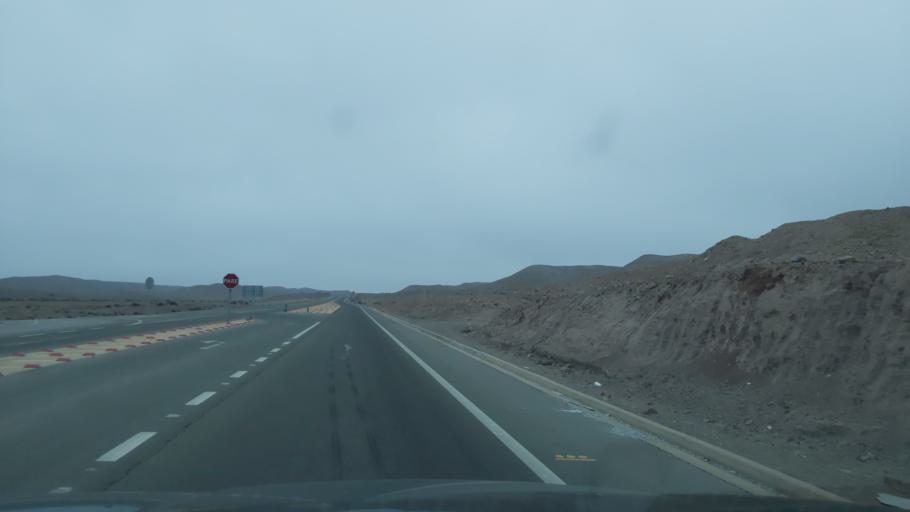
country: CL
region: Atacama
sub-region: Provincia de Copiapo
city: Copiapo
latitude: -27.2897
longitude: -70.1453
